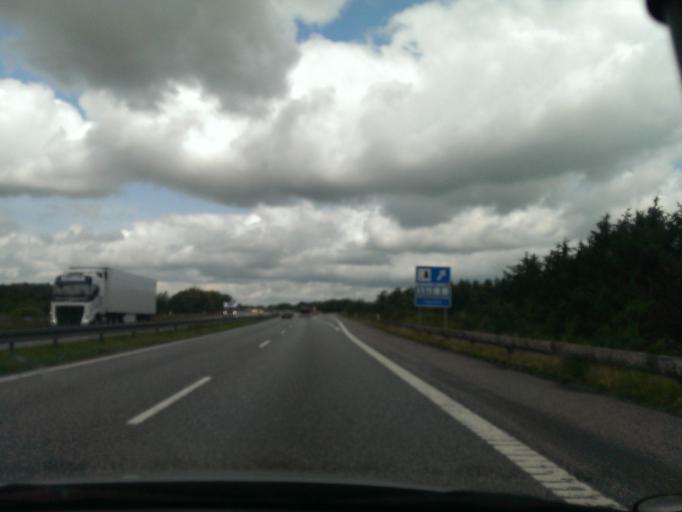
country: DK
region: North Denmark
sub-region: Mariagerfjord Kommune
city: Hobro
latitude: 56.5678
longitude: 9.8570
